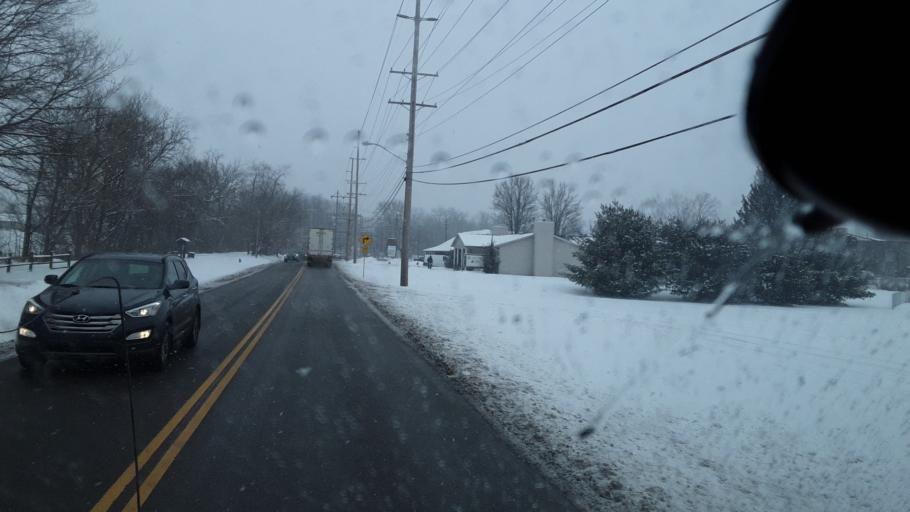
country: US
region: Ohio
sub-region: Licking County
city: Heath
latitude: 40.0442
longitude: -82.4728
